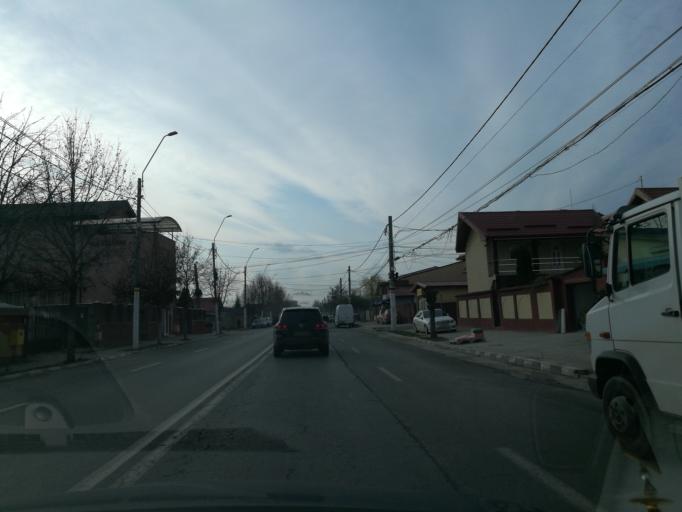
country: RO
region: Ilfov
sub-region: Voluntari City
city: Voluntari
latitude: 44.4925
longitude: 26.1722
